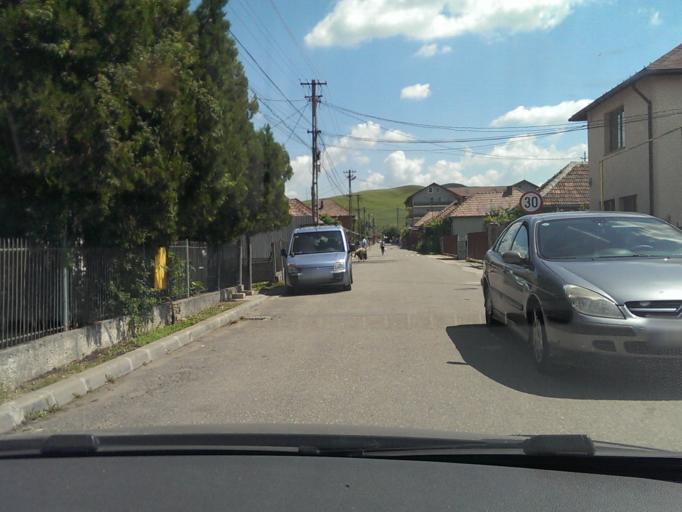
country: RO
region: Cluj
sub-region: Comuna Apahida
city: Sannicoara
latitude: 46.7962
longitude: 23.7437
